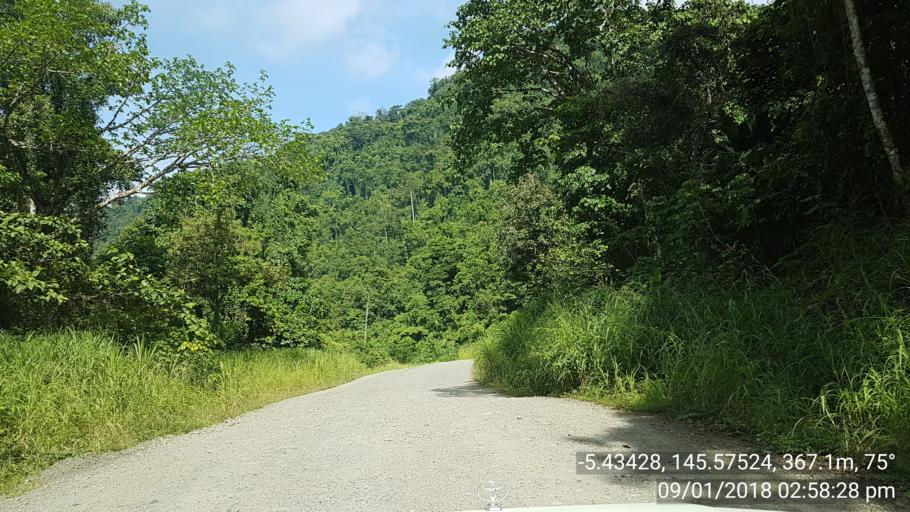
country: PG
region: Madang
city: Madang
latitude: -5.4344
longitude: 145.5753
